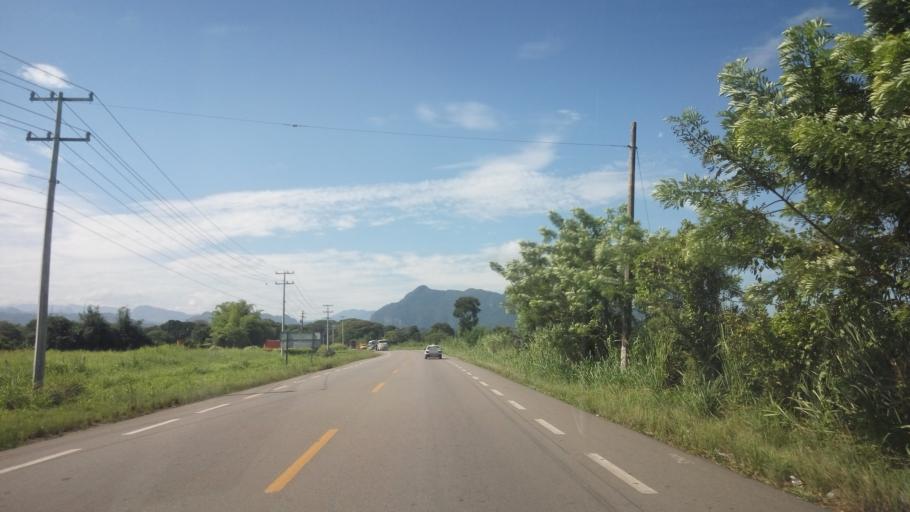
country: MX
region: Tabasco
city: Teapa
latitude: 17.5880
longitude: -92.9669
